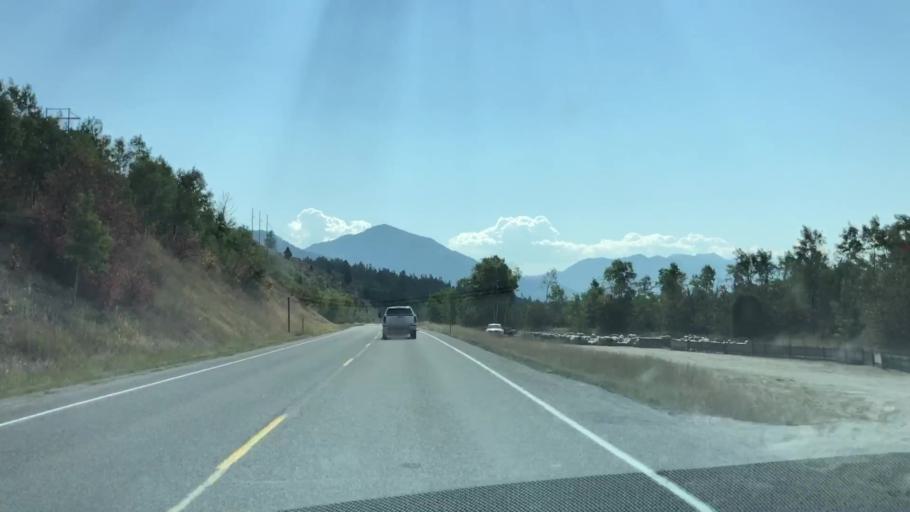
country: US
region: Wyoming
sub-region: Teton County
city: Hoback
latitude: 43.2059
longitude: -111.0518
